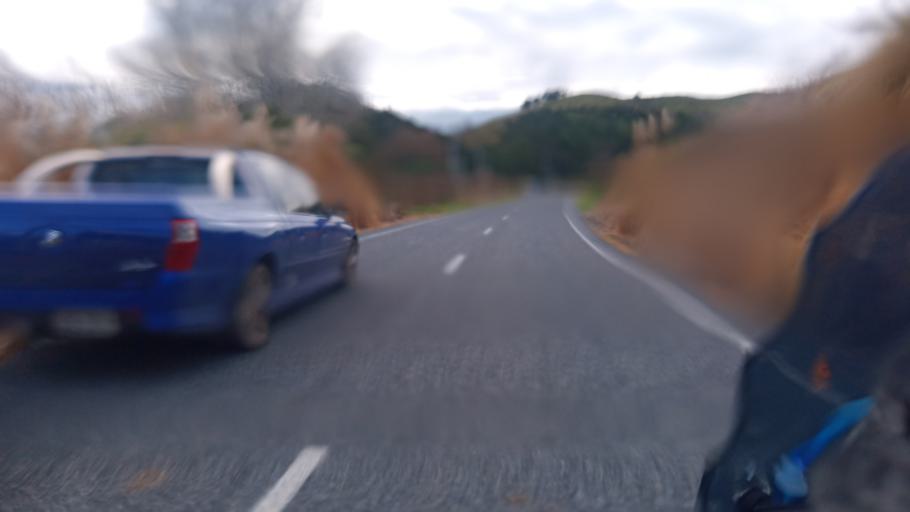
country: NZ
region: Gisborne
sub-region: Gisborne District
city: Gisborne
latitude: -38.4591
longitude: 177.8761
